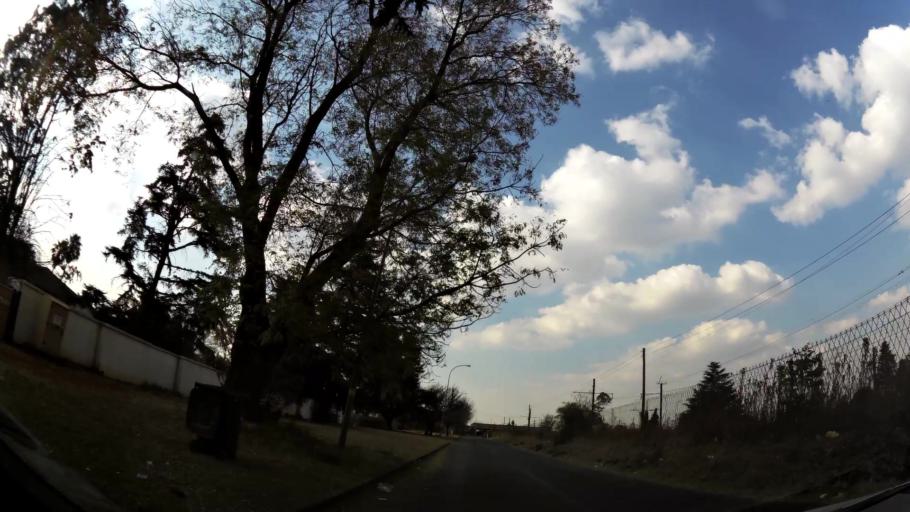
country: ZA
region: Gauteng
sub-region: Ekurhuleni Metropolitan Municipality
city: Germiston
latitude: -26.2504
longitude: 28.1812
